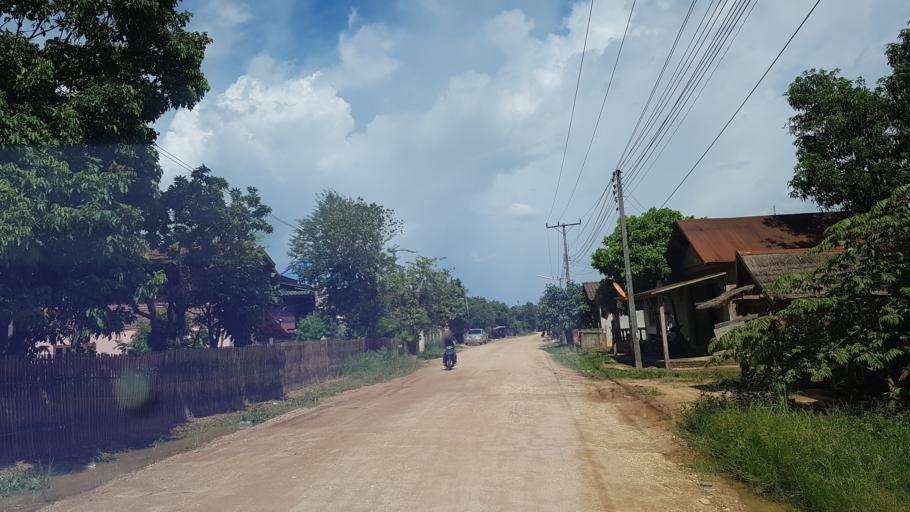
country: LA
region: Vientiane
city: Vientiane
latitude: 18.2159
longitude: 102.5131
